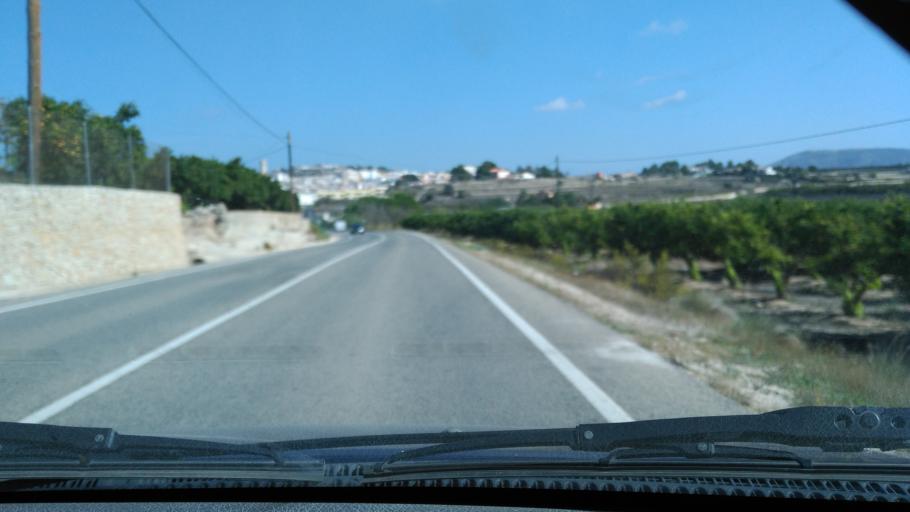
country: ES
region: Valencia
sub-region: Provincia de Alicante
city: Teulada
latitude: 38.7245
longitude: 0.0939
